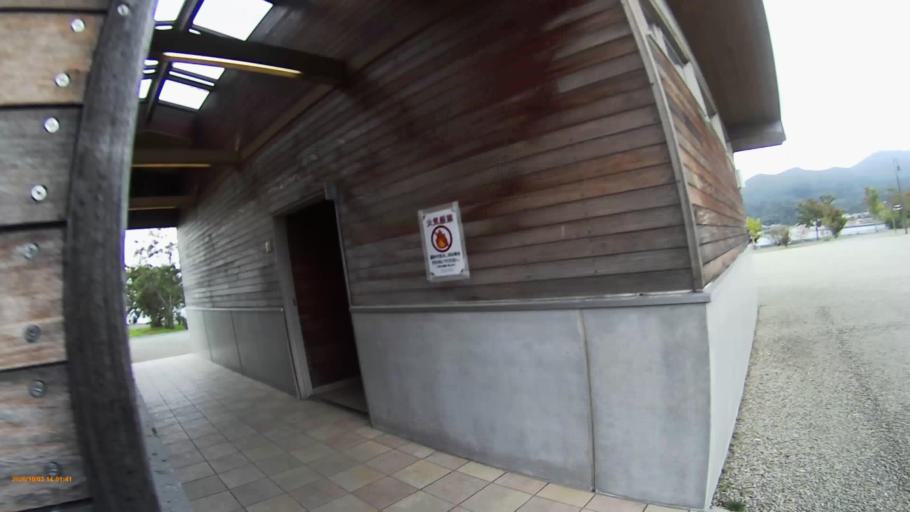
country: JP
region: Shizuoka
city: Gotemba
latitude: 35.4208
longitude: 138.9010
